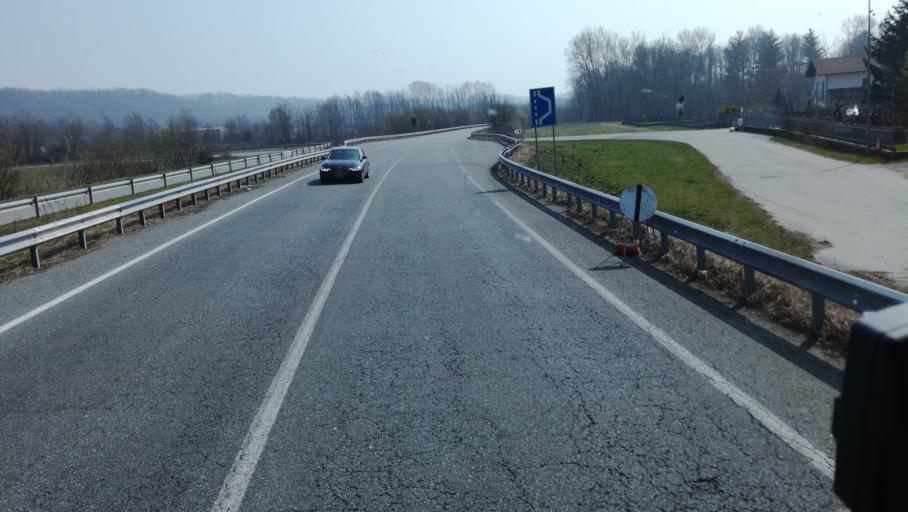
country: IT
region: Piedmont
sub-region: Provincia di Novara
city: Grignasco
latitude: 45.6685
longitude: 8.3592
